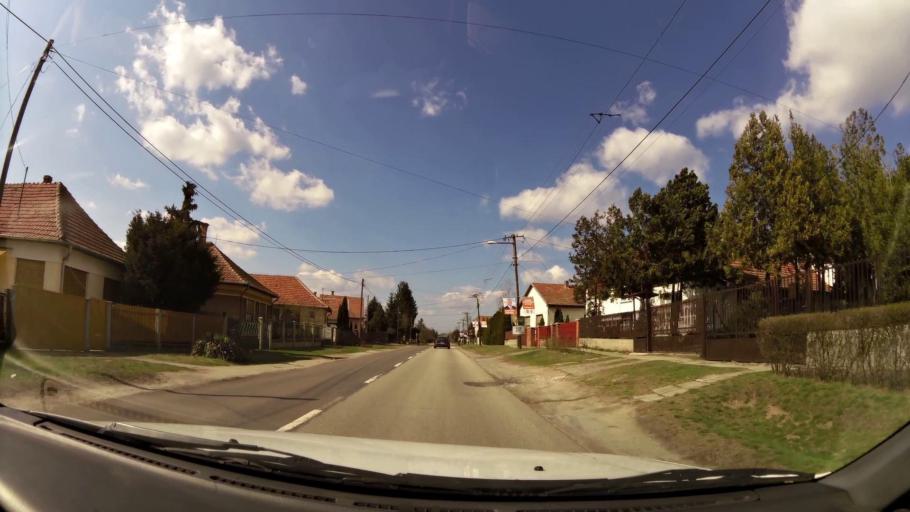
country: HU
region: Pest
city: Farmos
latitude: 47.3544
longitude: 19.8549
